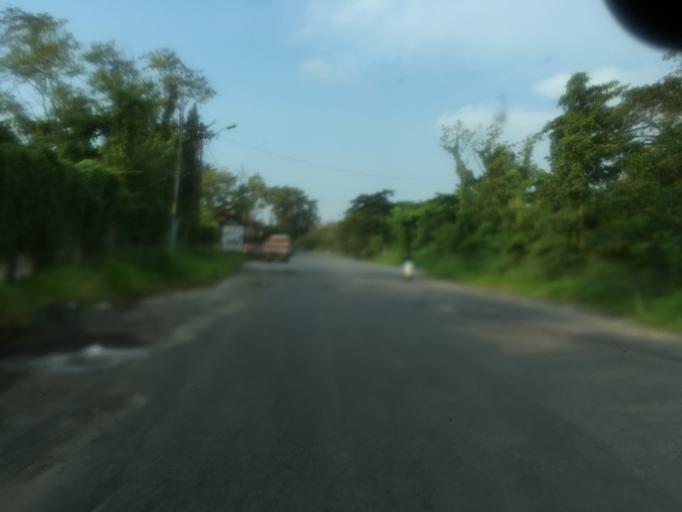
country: IN
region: Kerala
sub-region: Ernakulam
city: Cochin
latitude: 9.9535
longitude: 76.2684
